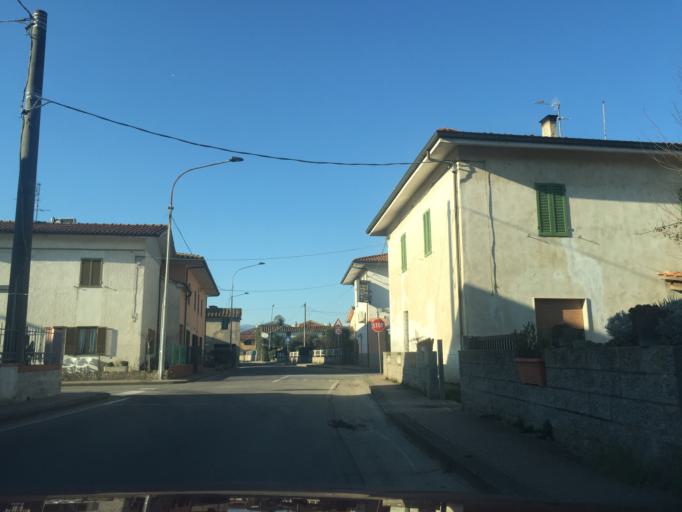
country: IT
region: Tuscany
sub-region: Provincia di Pistoia
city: Anchione
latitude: 43.8211
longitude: 10.7602
